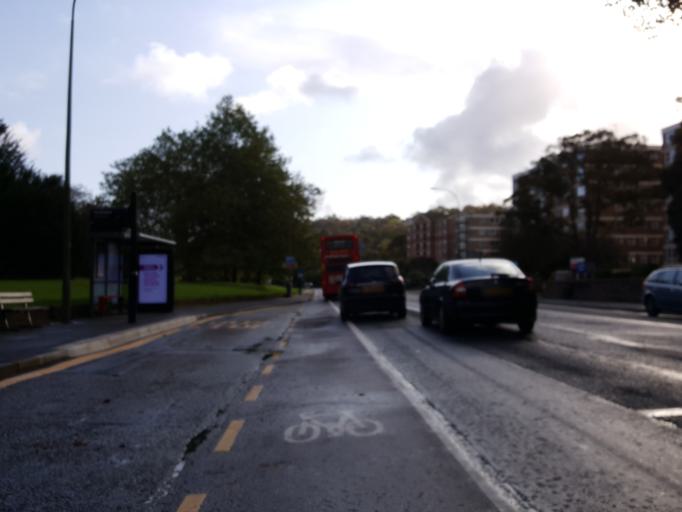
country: GB
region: England
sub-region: Brighton and Hove
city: Hove
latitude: 50.8557
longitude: -0.1542
